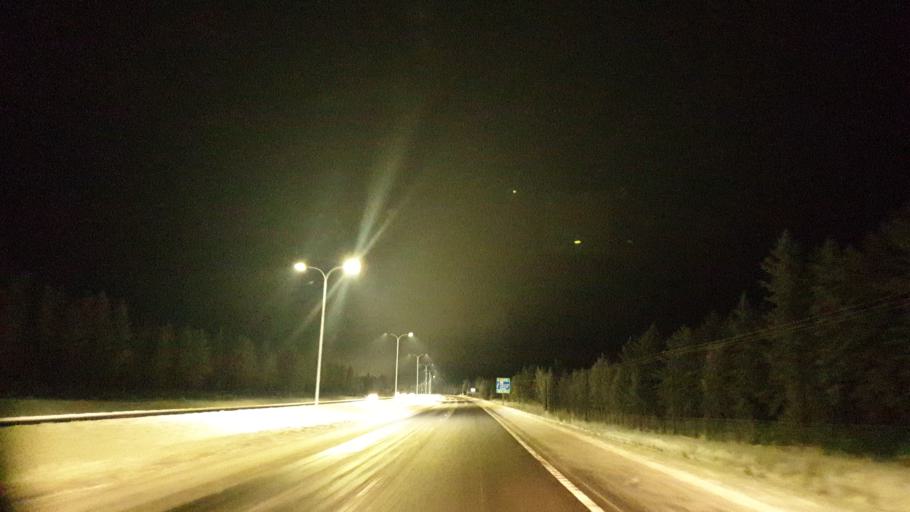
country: FI
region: Northern Ostrobothnia
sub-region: Oulu
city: Haukipudas
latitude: 65.1790
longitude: 25.4259
